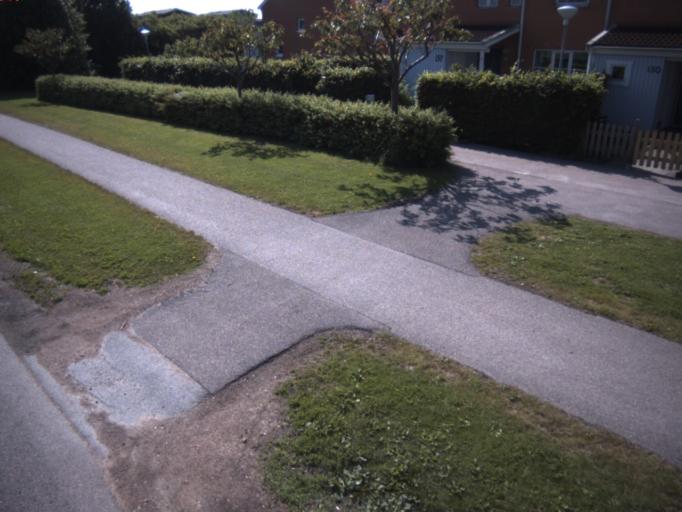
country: SE
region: Skane
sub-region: Helsingborg
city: Helsingborg
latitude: 56.0312
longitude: 12.7498
